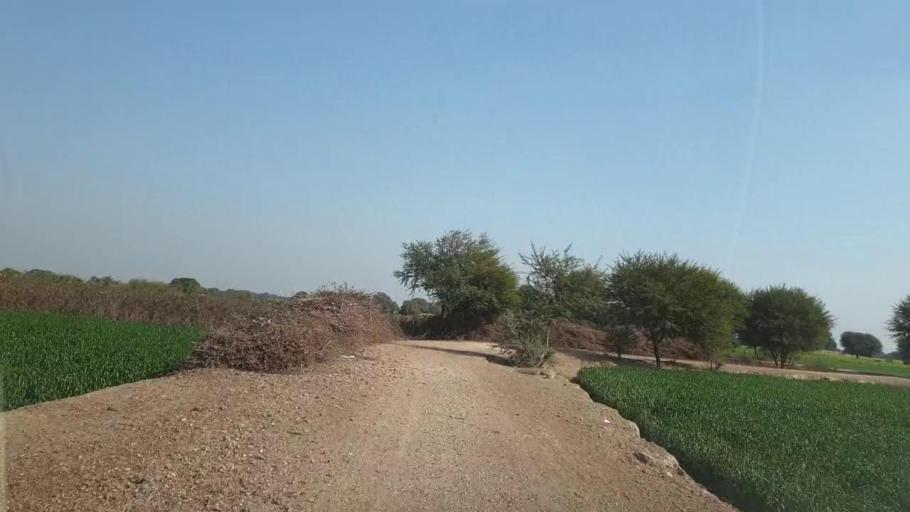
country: PK
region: Sindh
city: Tando Jam
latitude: 25.5040
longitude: 68.4990
